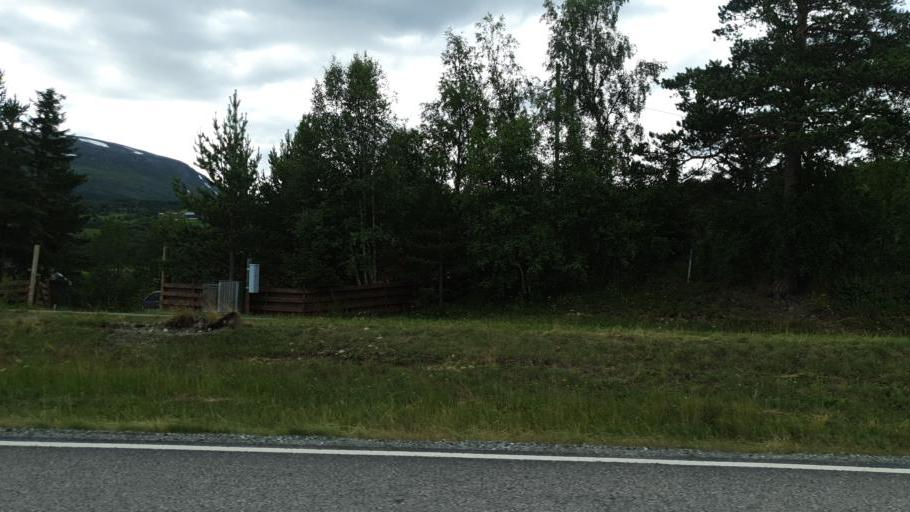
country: NO
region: Sor-Trondelag
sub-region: Oppdal
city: Oppdal
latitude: 62.5698
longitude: 9.6469
